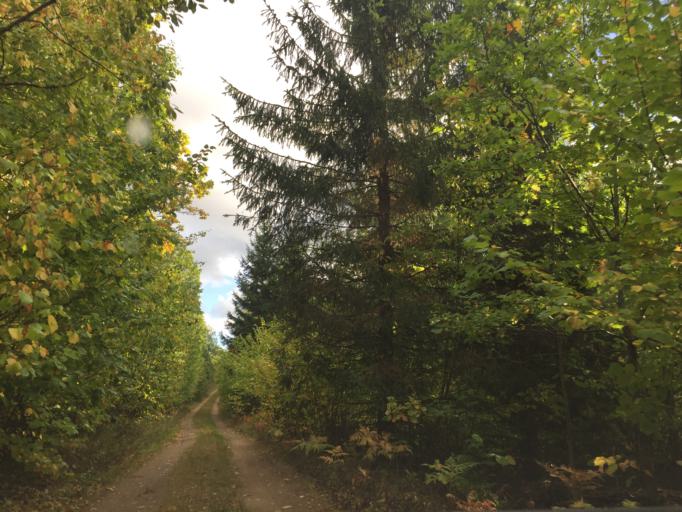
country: LV
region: Ligatne
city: Ligatne
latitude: 57.1167
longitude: 25.1362
